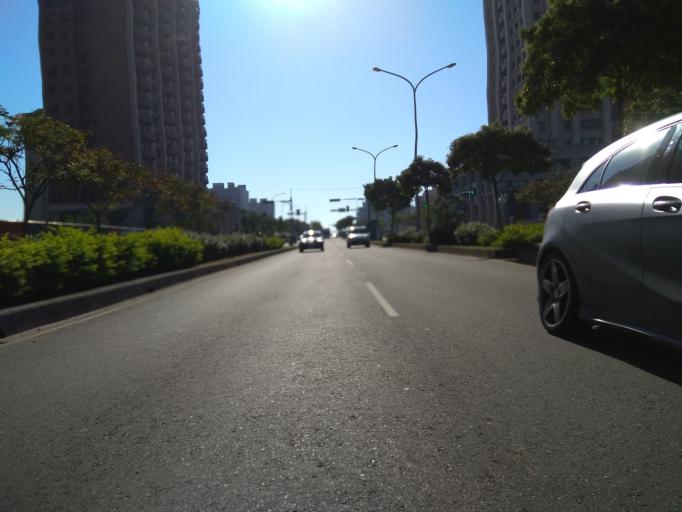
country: TW
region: Taiwan
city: Taoyuan City
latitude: 25.0092
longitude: 121.2189
